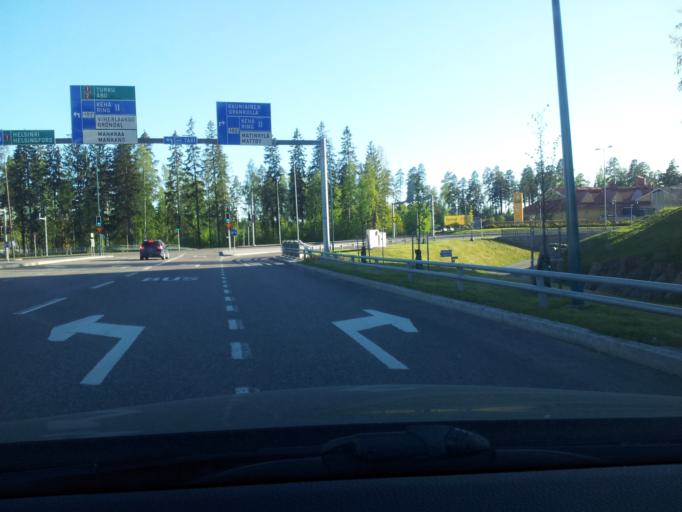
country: FI
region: Uusimaa
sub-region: Helsinki
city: Kauniainen
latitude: 60.2081
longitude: 24.7523
